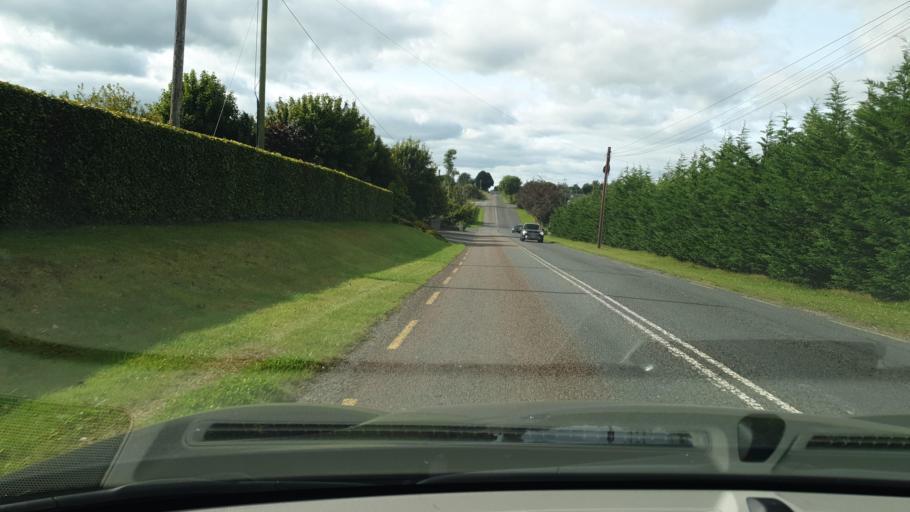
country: IE
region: Leinster
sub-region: Laois
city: Portlaoise
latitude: 53.0509
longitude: -7.2438
